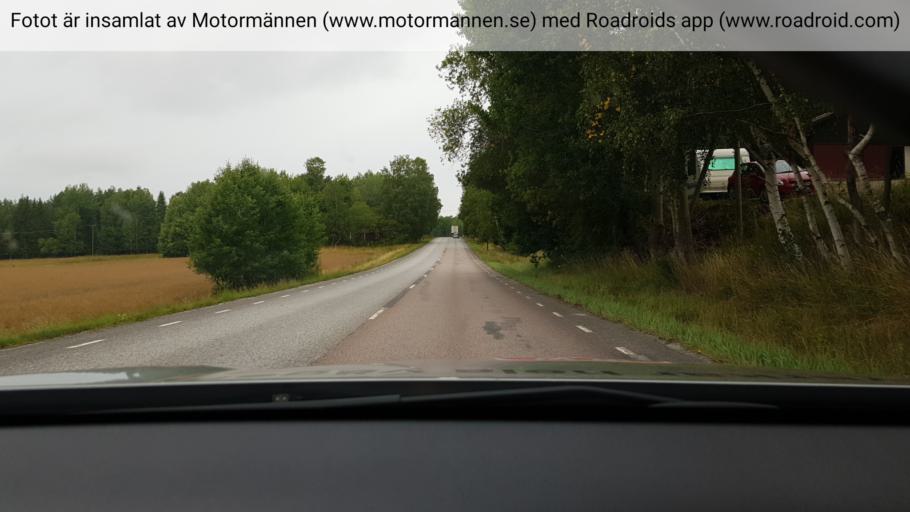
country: SE
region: Soedermanland
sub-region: Strangnas Kommun
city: Mariefred
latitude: 59.2233
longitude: 17.2250
